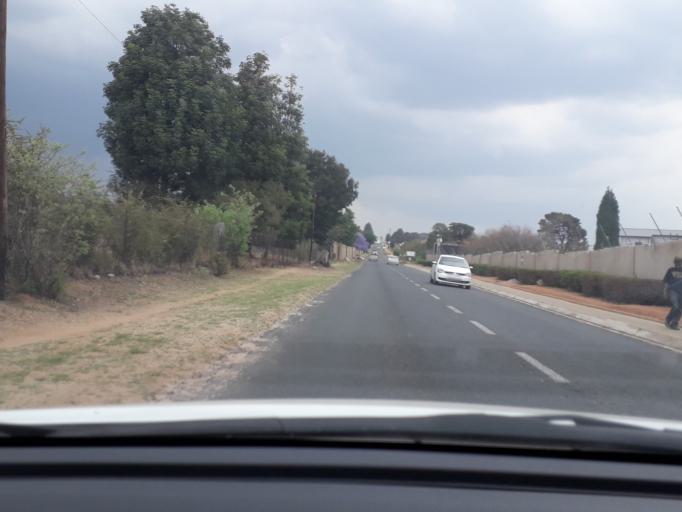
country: ZA
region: Gauteng
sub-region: West Rand District Municipality
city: Muldersdriseloop
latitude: -26.0629
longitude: 27.9257
